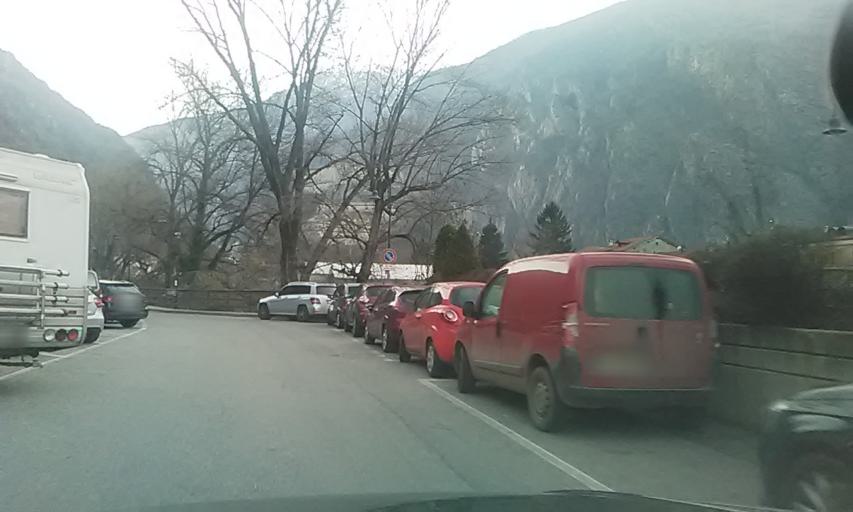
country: IT
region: Aosta Valley
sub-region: Valle d'Aosta
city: Hone
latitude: 45.6152
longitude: 7.7424
